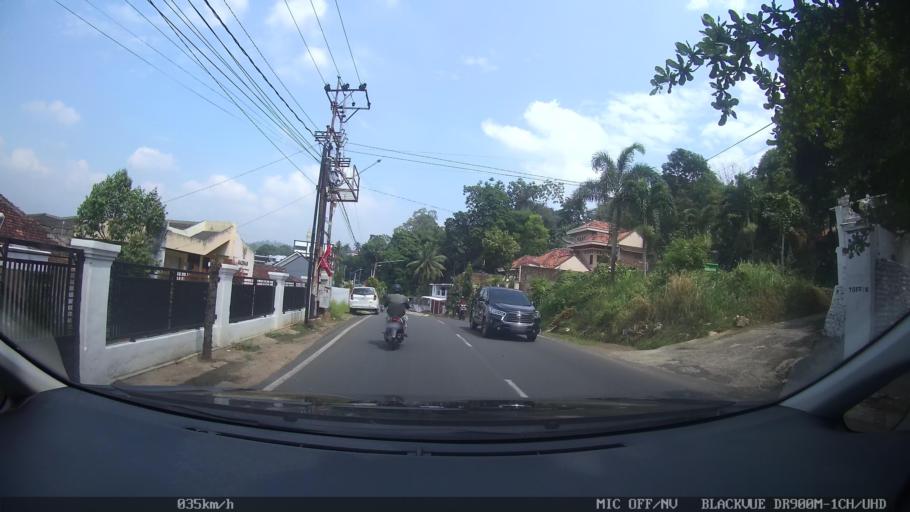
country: ID
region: Lampung
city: Bandarlampung
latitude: -5.4300
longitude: 105.2562
